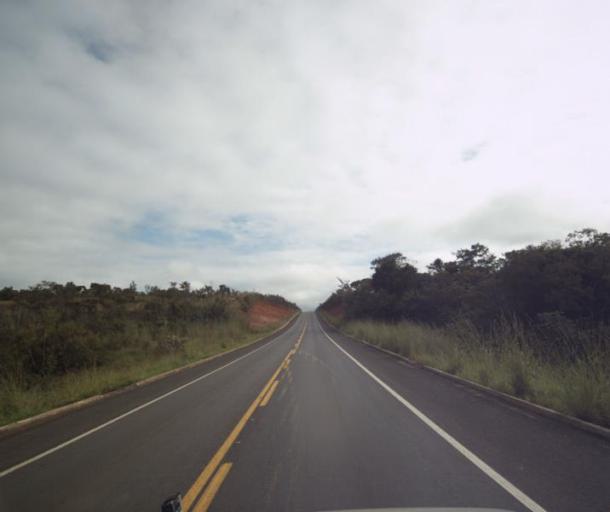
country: BR
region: Goias
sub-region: Padre Bernardo
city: Padre Bernardo
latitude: -15.3683
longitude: -48.6459
